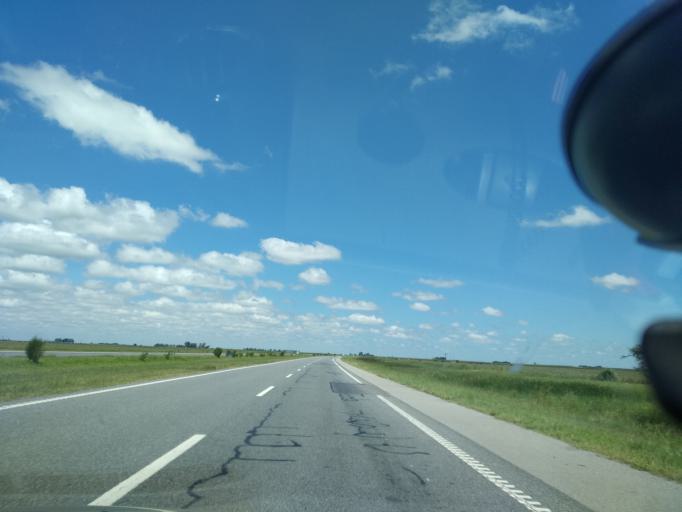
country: AR
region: Cordoba
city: Oliva
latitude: -32.0497
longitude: -63.5100
